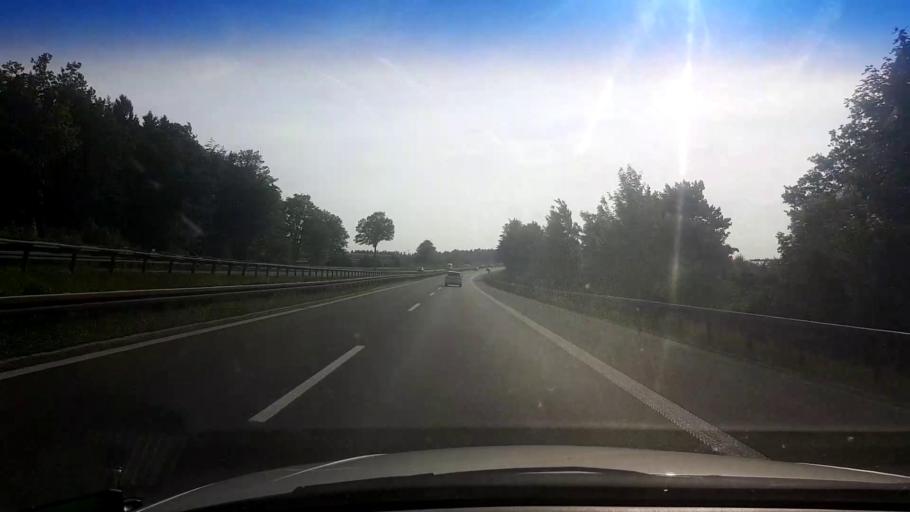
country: DE
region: Bavaria
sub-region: Upper Franconia
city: Wonsees
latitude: 50.0069
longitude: 11.2700
